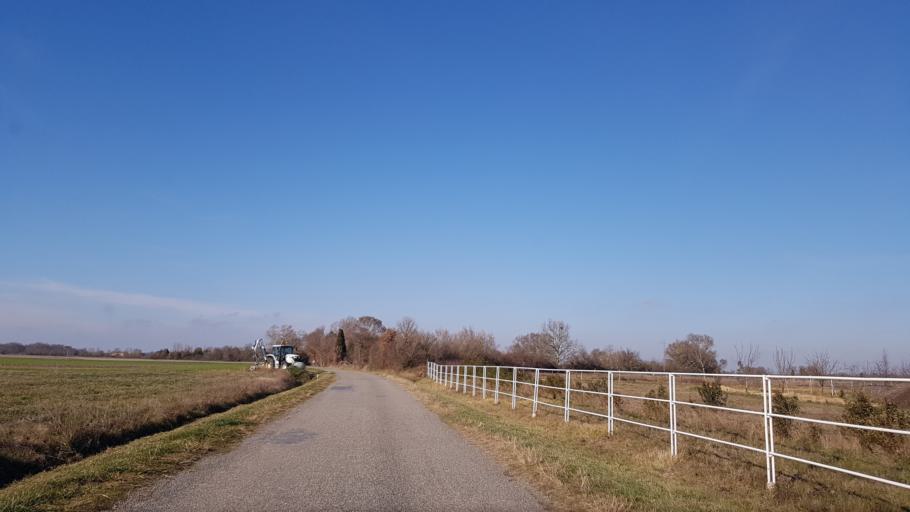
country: FR
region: Midi-Pyrenees
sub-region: Departement de l'Ariege
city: La Tour-du-Crieu
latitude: 43.1577
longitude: 1.6843
